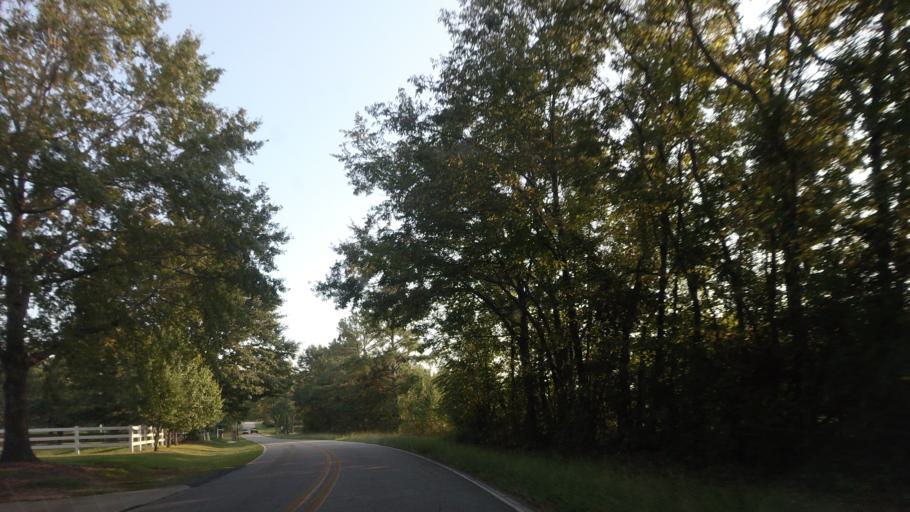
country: US
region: Georgia
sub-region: Bibb County
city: West Point
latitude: 32.9481
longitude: -83.8077
